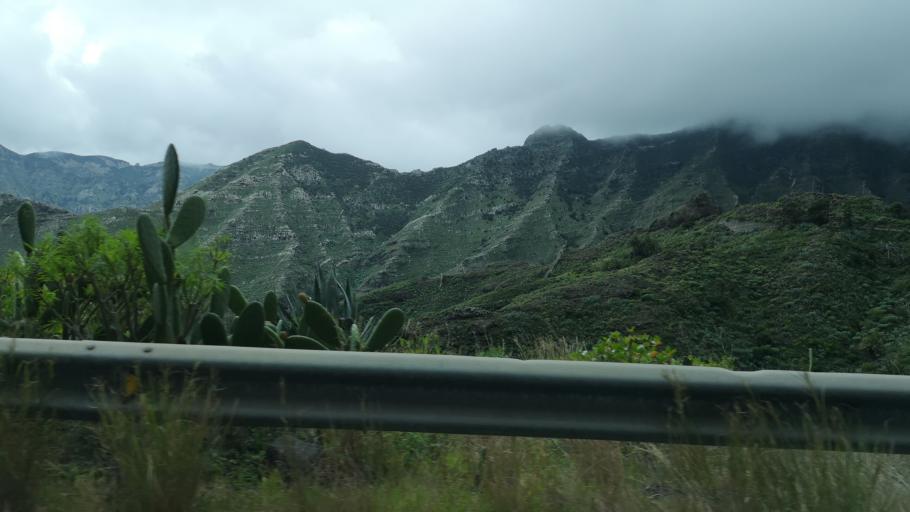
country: ES
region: Canary Islands
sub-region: Provincia de Santa Cruz de Tenerife
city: Hermigua
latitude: 28.1322
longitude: -17.1798
